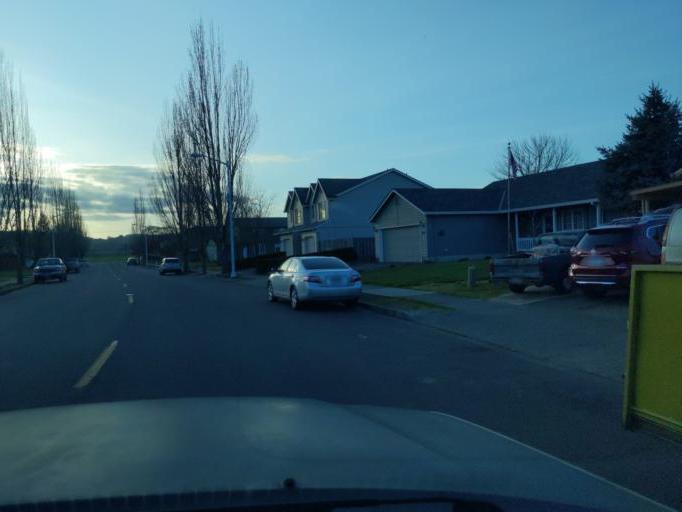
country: US
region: Oregon
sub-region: Yamhill County
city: McMinnville
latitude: 45.2021
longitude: -123.2272
